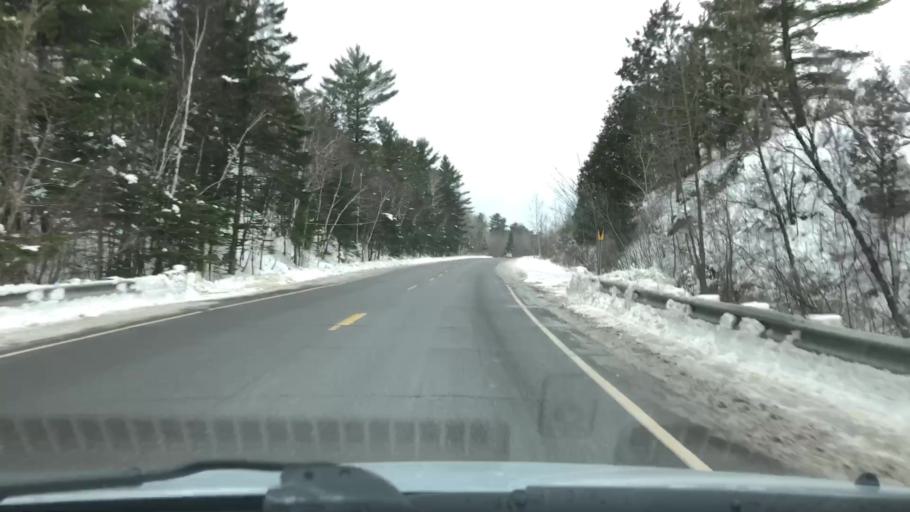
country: US
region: Minnesota
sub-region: Carlton County
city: Carlton
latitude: 46.6647
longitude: -92.4062
